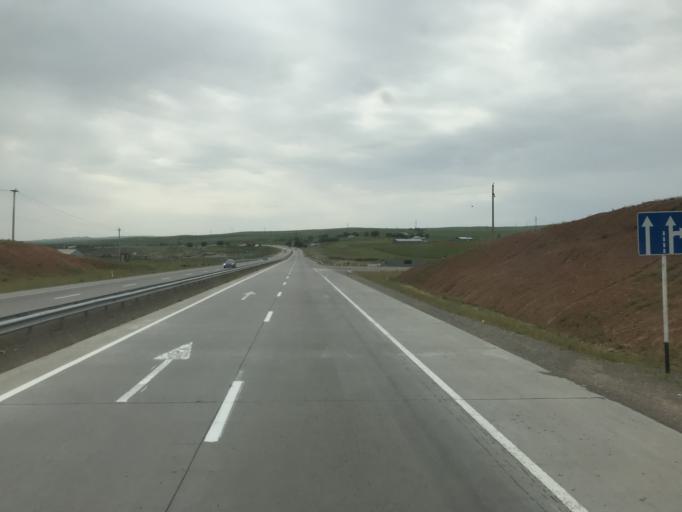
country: KZ
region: Ongtustik Qazaqstan
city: Qazyqurt
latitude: 41.8714
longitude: 69.4231
